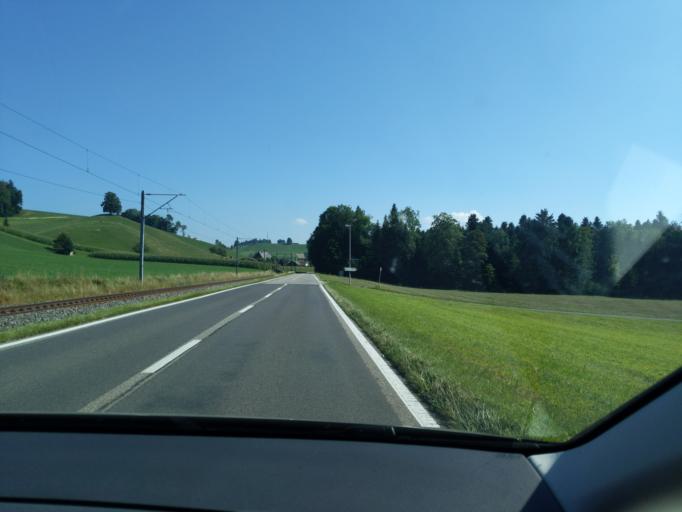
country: CH
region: Bern
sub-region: Oberaargau
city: Rohrbach
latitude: 47.1236
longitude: 7.8293
